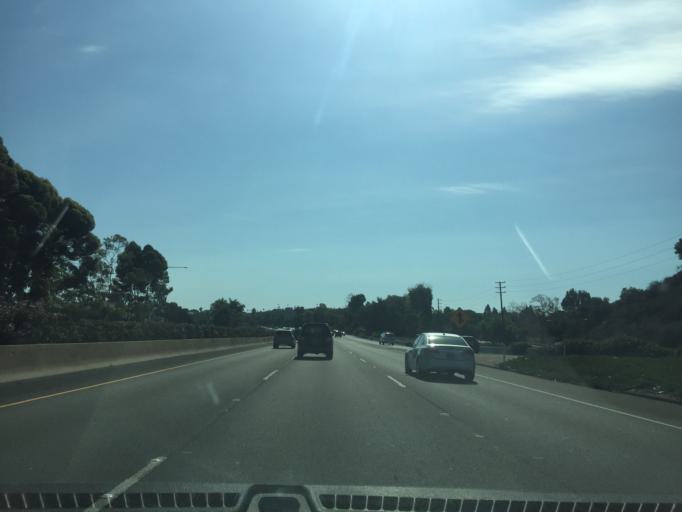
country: US
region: California
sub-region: Santa Barbara County
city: Mission Canyon
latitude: 34.4357
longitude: -119.7506
